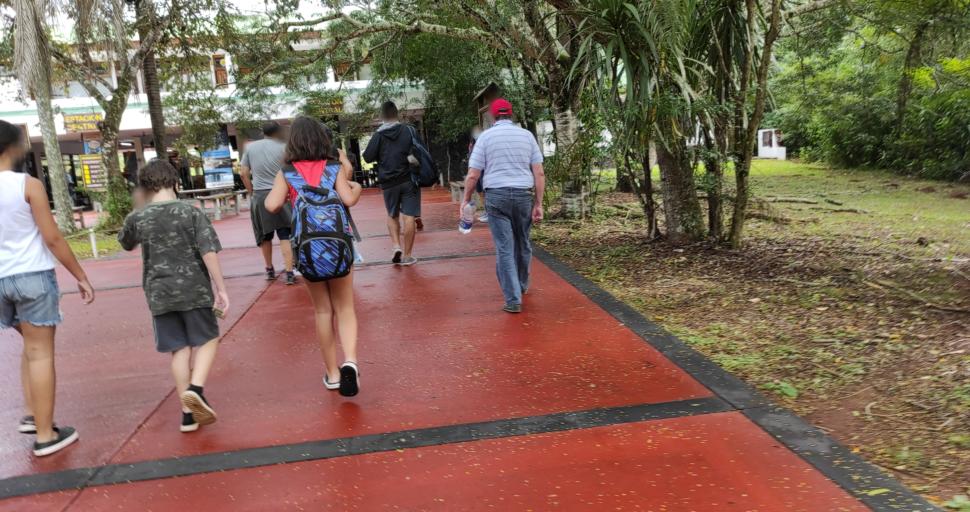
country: AR
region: Misiones
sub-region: Departamento de Iguazu
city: Puerto Iguazu
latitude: -25.6795
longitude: -54.4531
